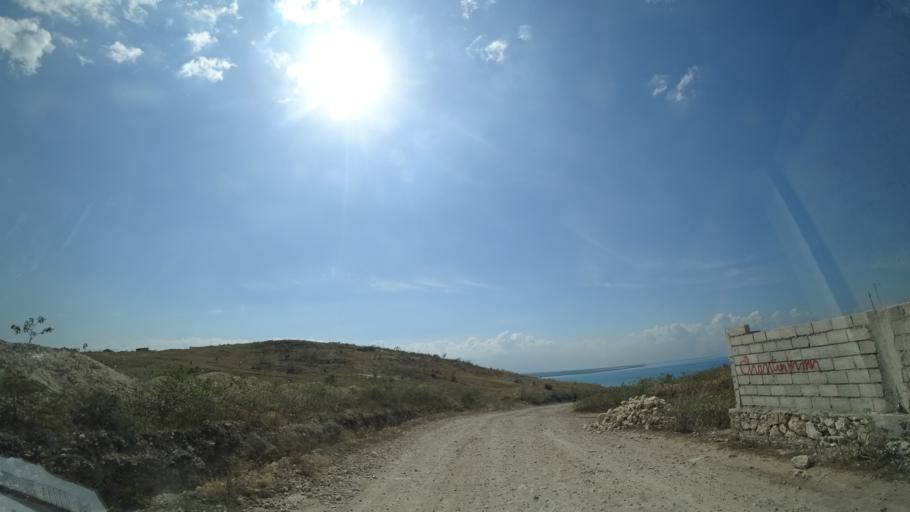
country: HT
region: Ouest
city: Cabaret
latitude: 18.6836
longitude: -72.3182
